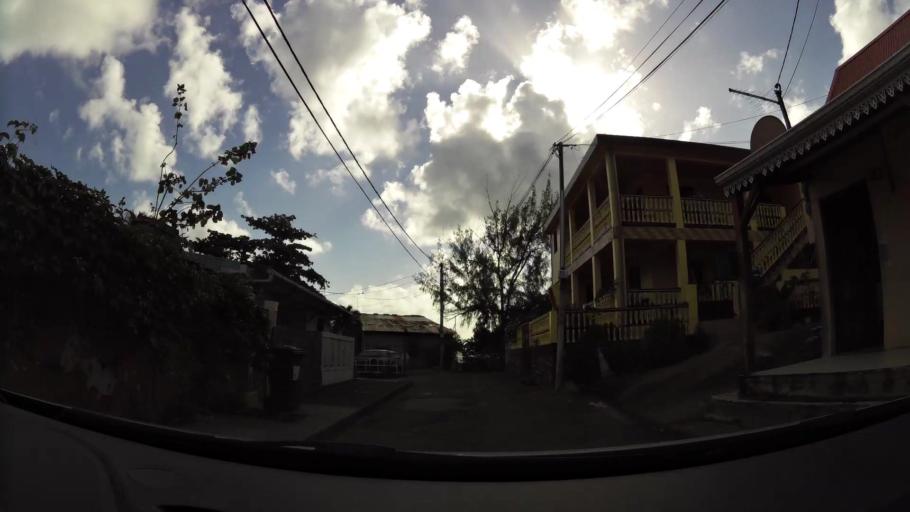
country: MQ
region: Martinique
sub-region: Martinique
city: Le Robert
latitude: 14.6819
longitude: -60.9378
